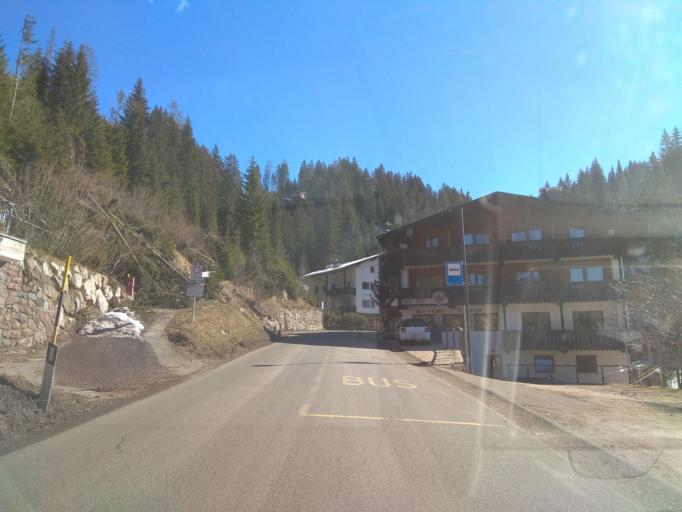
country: IT
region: Trentino-Alto Adige
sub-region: Bolzano
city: Nova Levante
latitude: 46.4169
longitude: 11.5687
